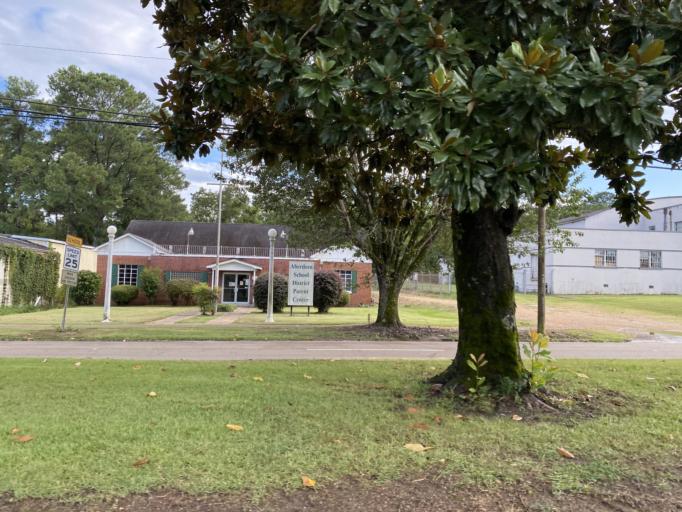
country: US
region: Mississippi
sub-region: Monroe County
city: Aberdeen
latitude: 33.8255
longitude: -88.5516
